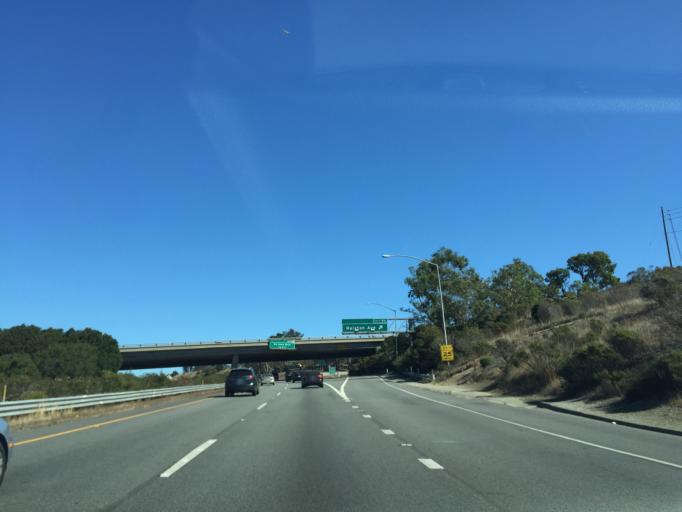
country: US
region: California
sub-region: San Mateo County
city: Highlands-Baywood Park
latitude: 37.5116
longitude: -122.3311
